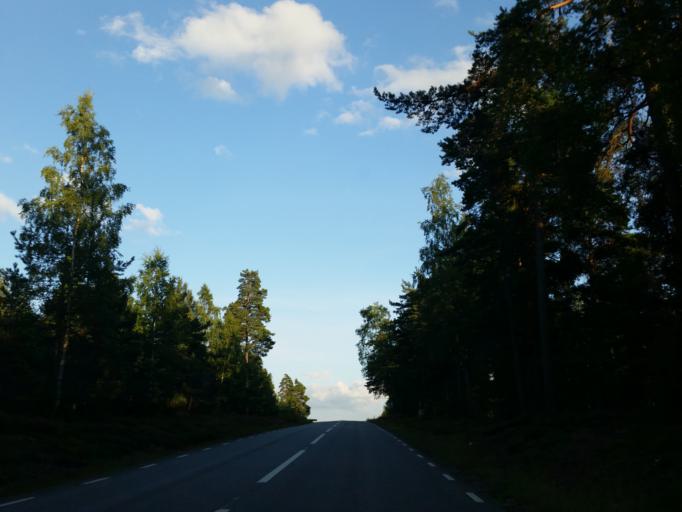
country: SE
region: Stockholm
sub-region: Sodertalje Kommun
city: Soedertaelje
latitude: 59.2320
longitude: 17.5498
